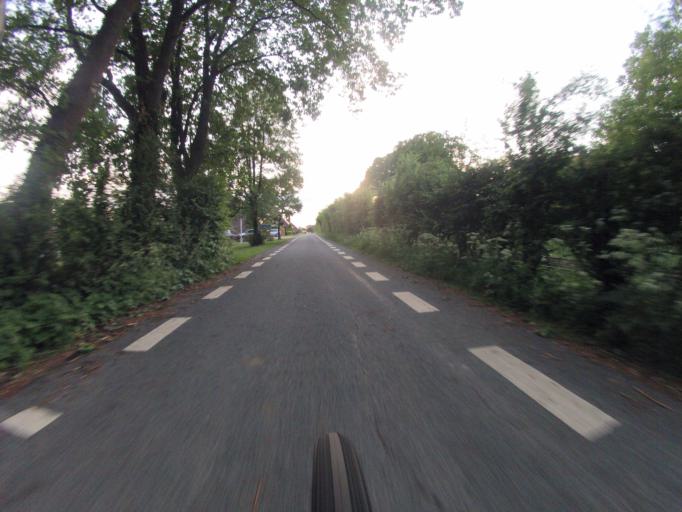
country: DE
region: North Rhine-Westphalia
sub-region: Regierungsbezirk Munster
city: Mettingen
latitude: 52.2657
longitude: 7.7776
